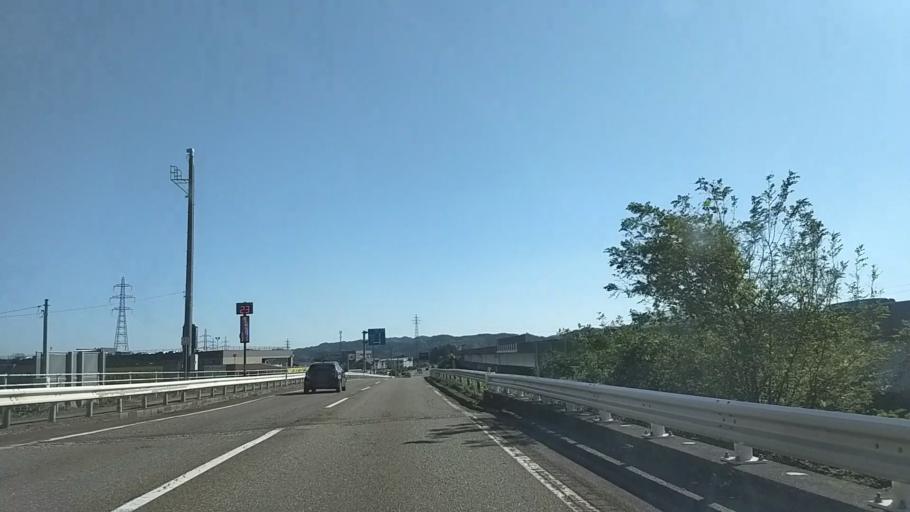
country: JP
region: Ishikawa
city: Kanazawa-shi
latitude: 36.6056
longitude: 136.6675
